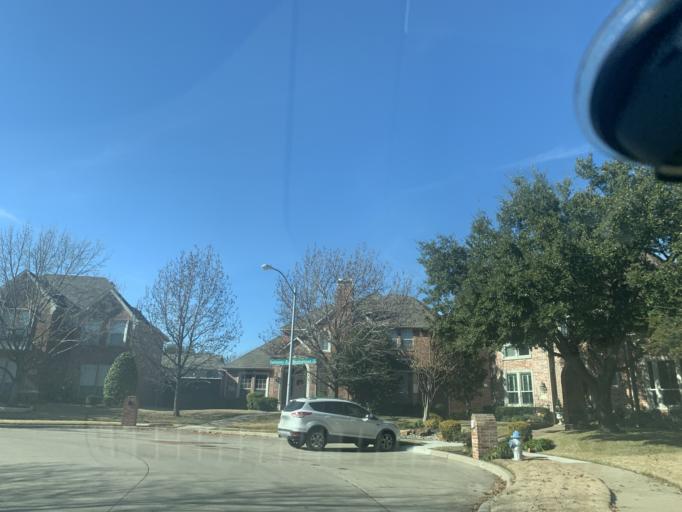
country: US
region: Texas
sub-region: Denton County
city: The Colony
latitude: 33.0526
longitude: -96.8201
